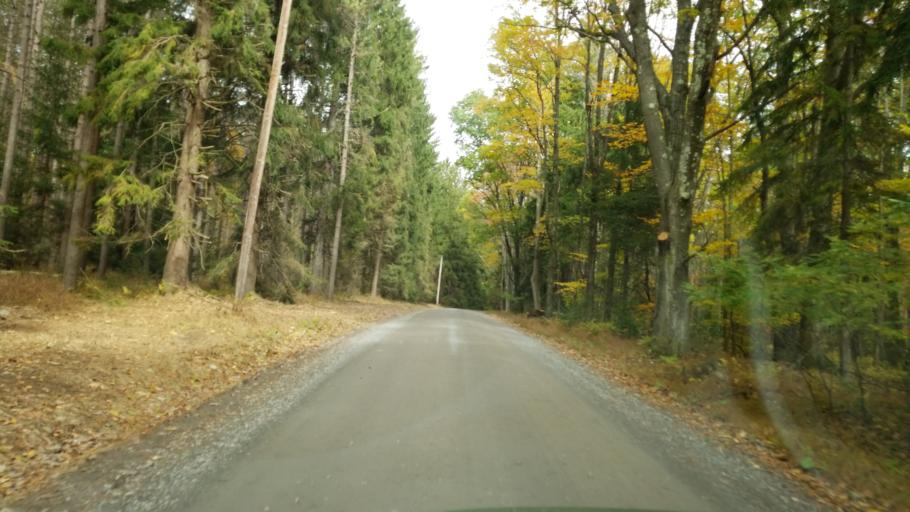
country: US
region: Pennsylvania
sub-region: Clearfield County
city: Clearfield
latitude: 41.1900
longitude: -78.4426
